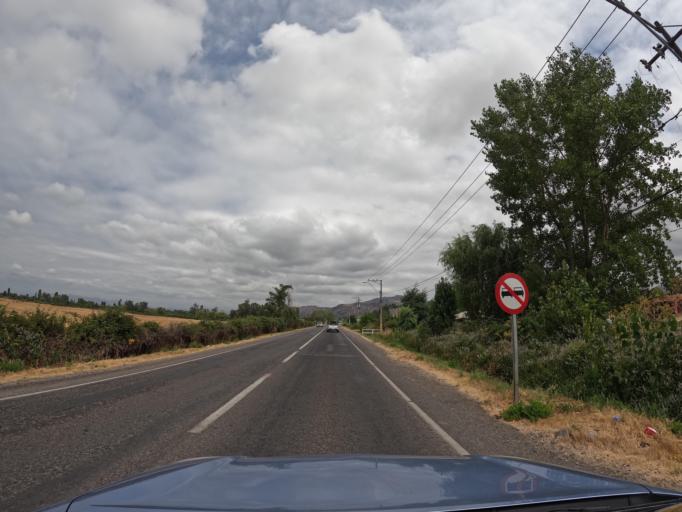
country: CL
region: Maule
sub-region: Provincia de Curico
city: Teno
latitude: -34.8624
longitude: -71.1795
